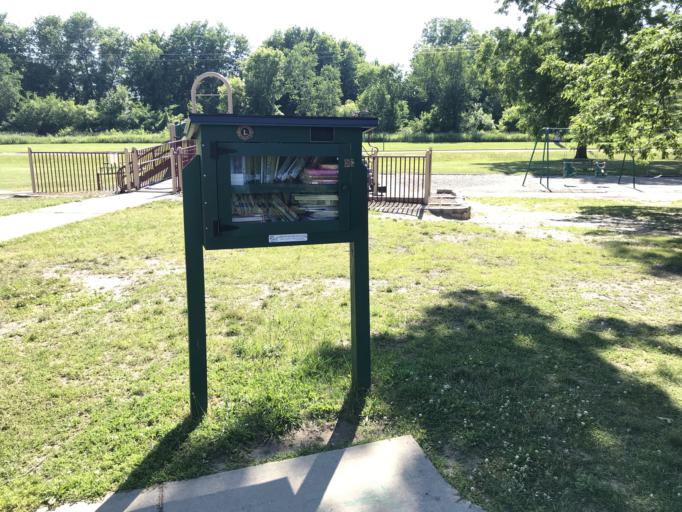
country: US
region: Michigan
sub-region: Ingham County
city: Holt
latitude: 42.6494
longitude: -84.5077
